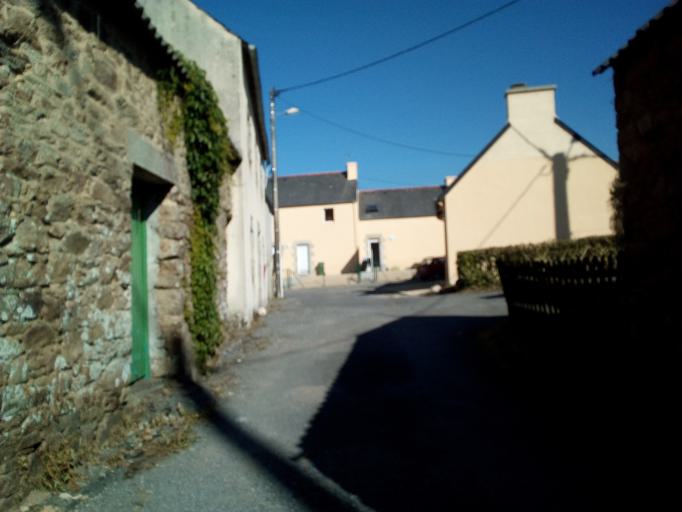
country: FR
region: Brittany
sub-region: Departement du Finistere
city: Landivisiau
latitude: 48.5056
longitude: -4.0765
